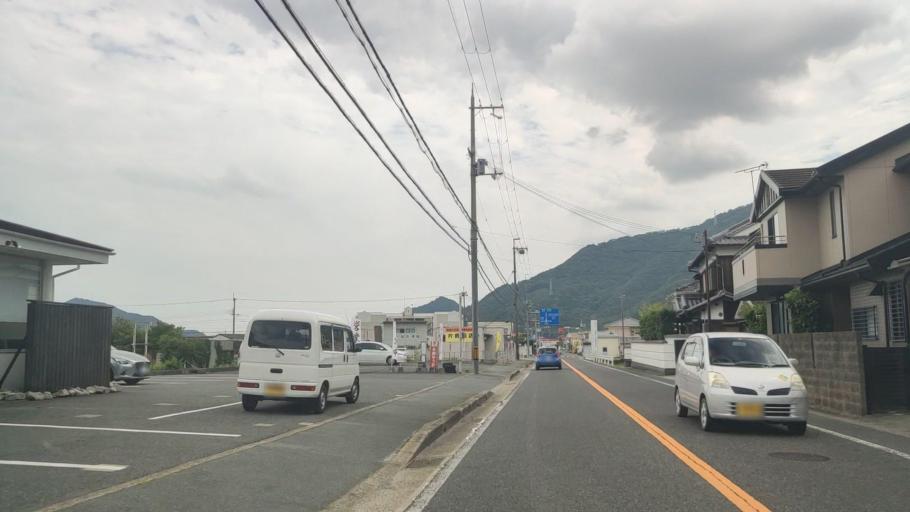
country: JP
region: Hyogo
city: Tatsunocho-tominaga
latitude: 34.8986
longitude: 134.5470
